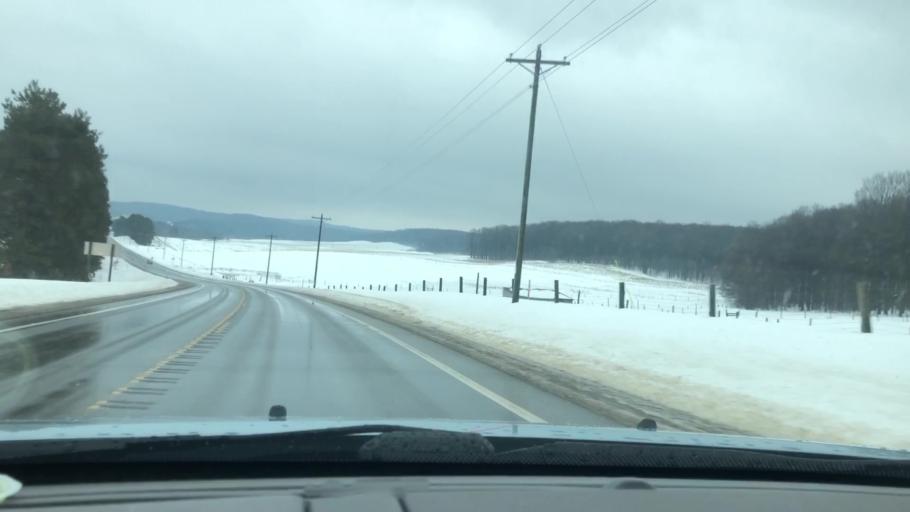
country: US
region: Michigan
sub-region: Charlevoix County
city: Boyne City
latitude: 45.0948
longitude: -84.9768
